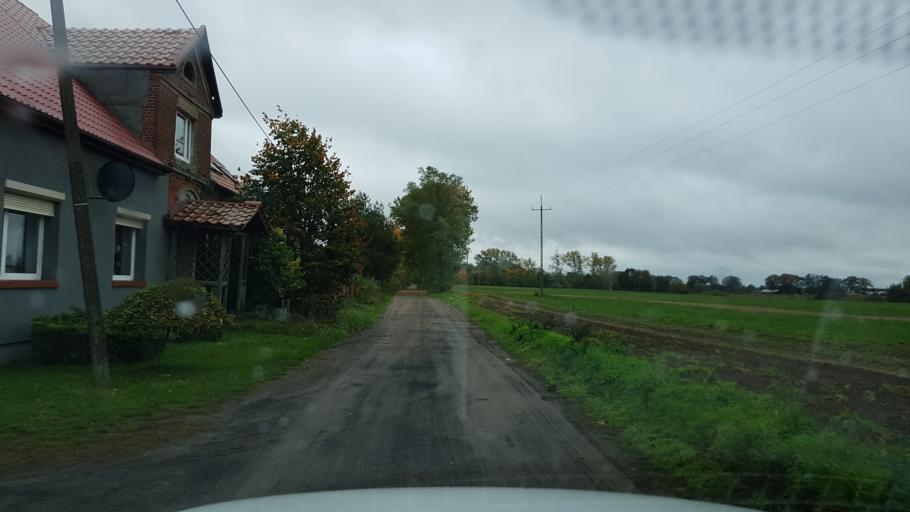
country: PL
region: West Pomeranian Voivodeship
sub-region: Powiat pyrzycki
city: Lipiany
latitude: 52.9759
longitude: 15.0105
